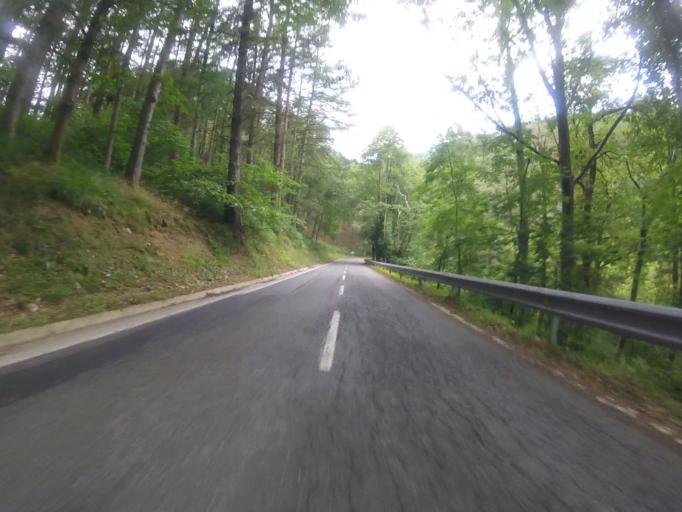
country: ES
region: Navarre
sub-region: Provincia de Navarra
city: Ezkurra
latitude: 43.0844
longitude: -1.8507
